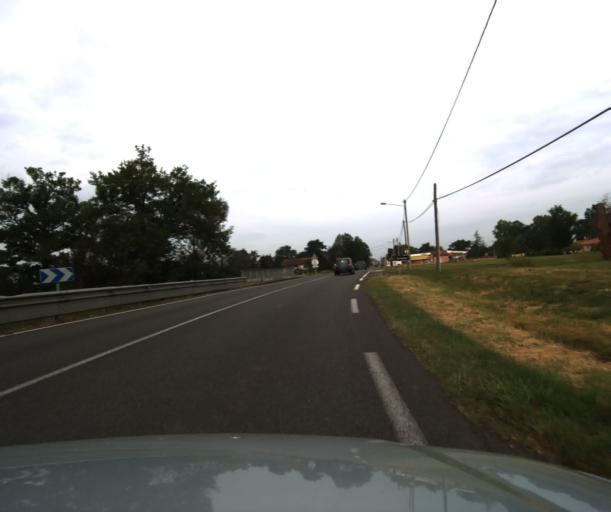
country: FR
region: Midi-Pyrenees
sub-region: Departement des Hautes-Pyrenees
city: Rabastens-de-Bigorre
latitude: 43.3893
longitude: 0.1603
